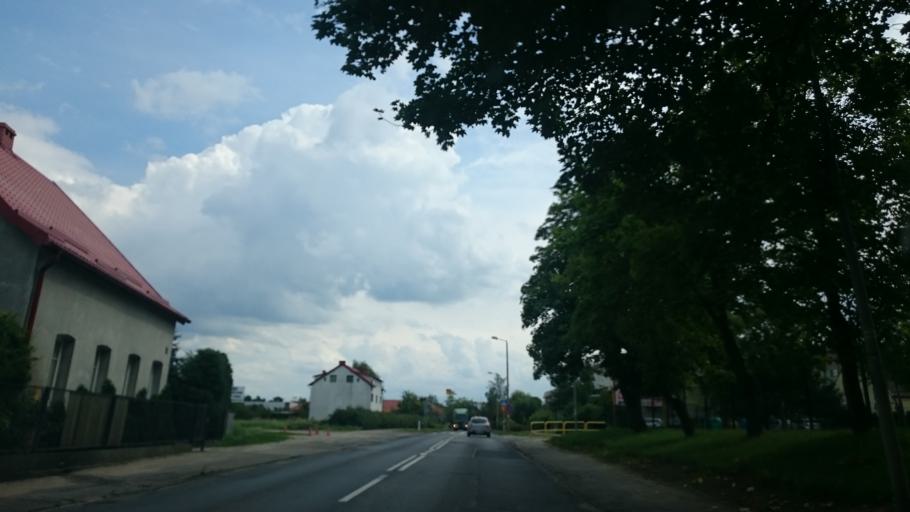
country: PL
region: Kujawsko-Pomorskie
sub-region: Powiat tucholski
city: Tuchola
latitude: 53.5891
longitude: 17.8674
